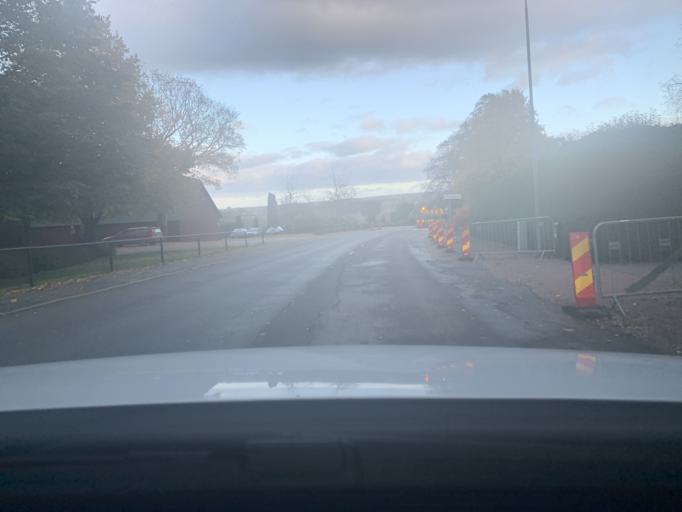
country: SE
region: Skane
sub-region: Horby Kommun
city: Hoerby
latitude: 55.8432
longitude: 13.6548
